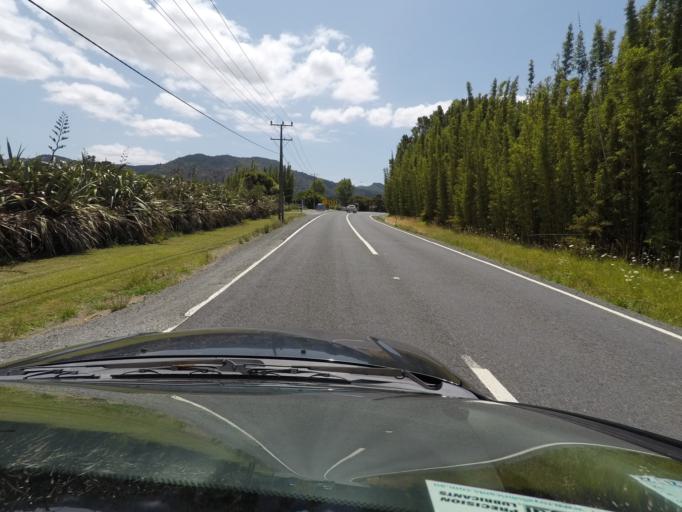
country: NZ
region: Auckland
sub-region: Auckland
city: Warkworth
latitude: -36.3235
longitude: 174.7312
